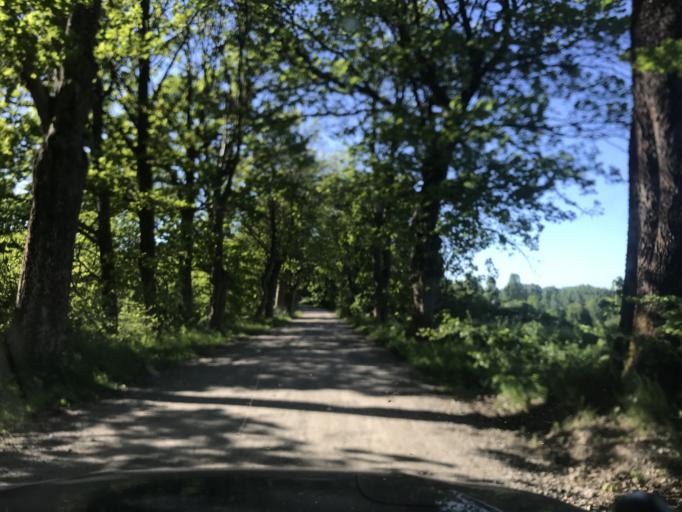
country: PL
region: West Pomeranian Voivodeship
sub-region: Powiat swidwinski
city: Polczyn-Zdroj
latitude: 53.7171
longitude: 16.1107
